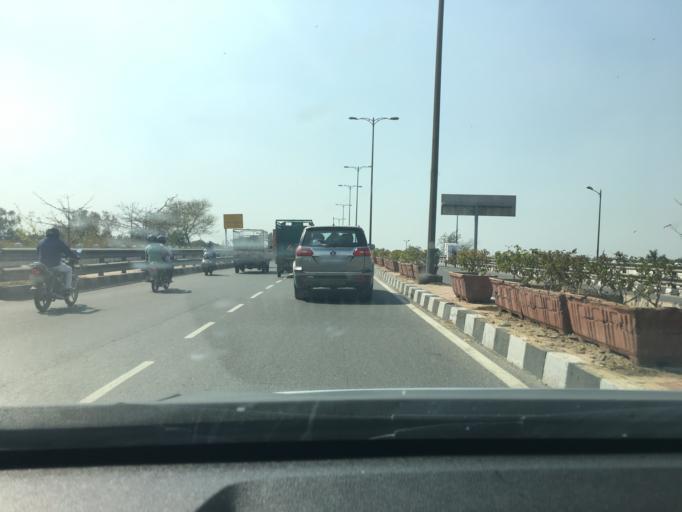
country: IN
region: NCT
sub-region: North Delhi
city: Delhi
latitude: 28.6513
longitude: 77.2532
